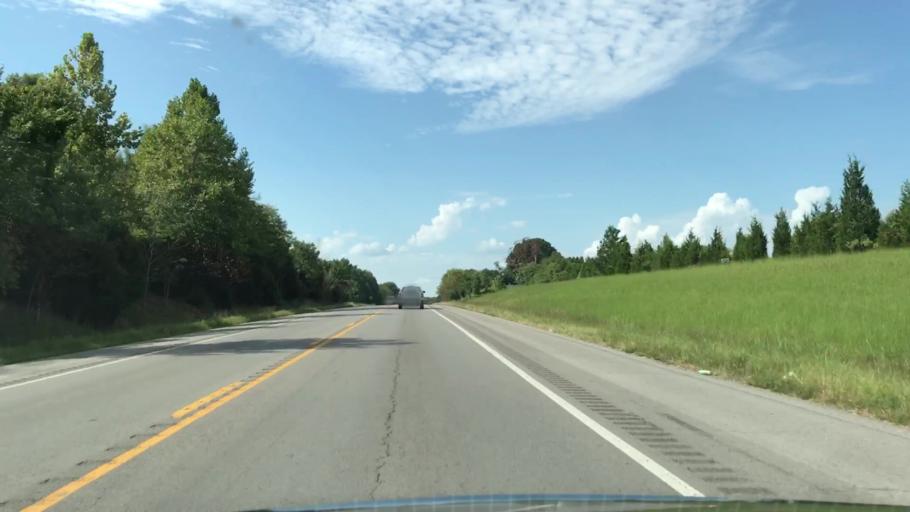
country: US
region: Kentucky
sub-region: Allen County
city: Scottsville
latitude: 36.7314
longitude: -86.2231
